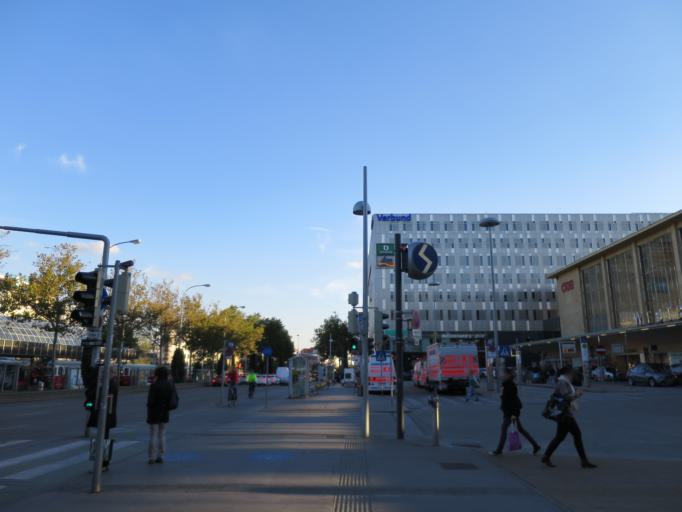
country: AT
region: Vienna
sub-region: Wien Stadt
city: Vienna
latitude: 48.1975
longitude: 16.3384
